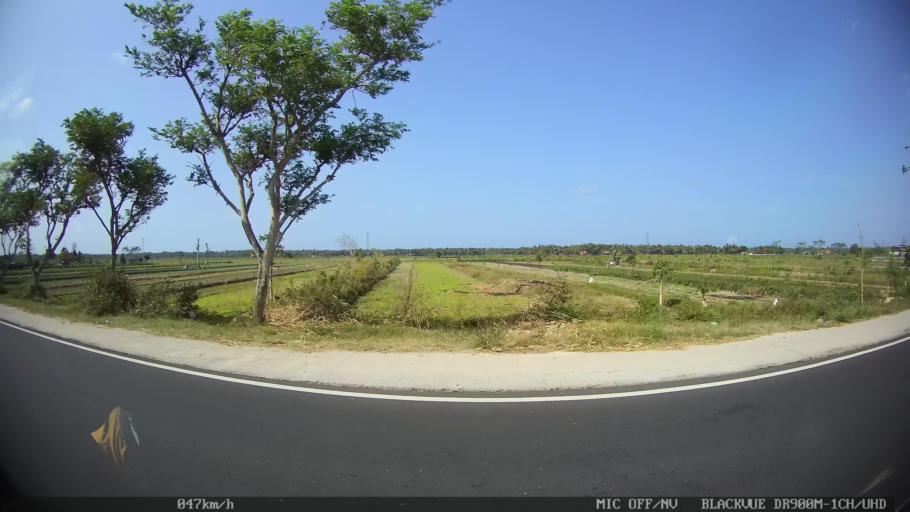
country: ID
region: Daerah Istimewa Yogyakarta
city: Srandakan
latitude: -7.8966
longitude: 110.1580
